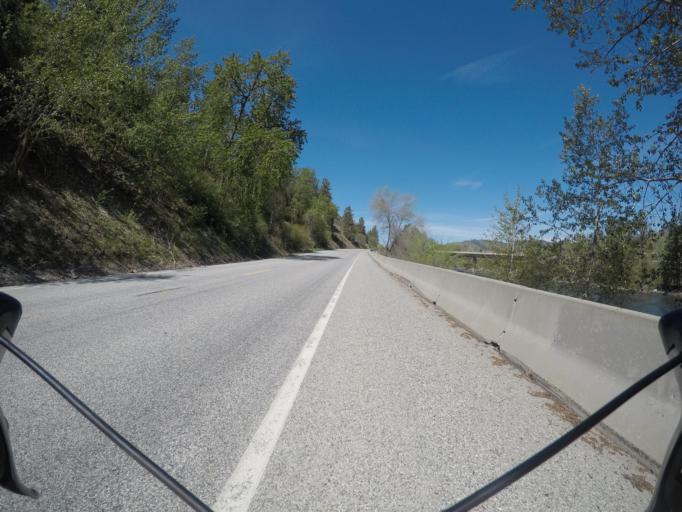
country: US
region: Washington
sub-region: Chelan County
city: Cashmere
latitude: 47.5336
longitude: -120.5499
